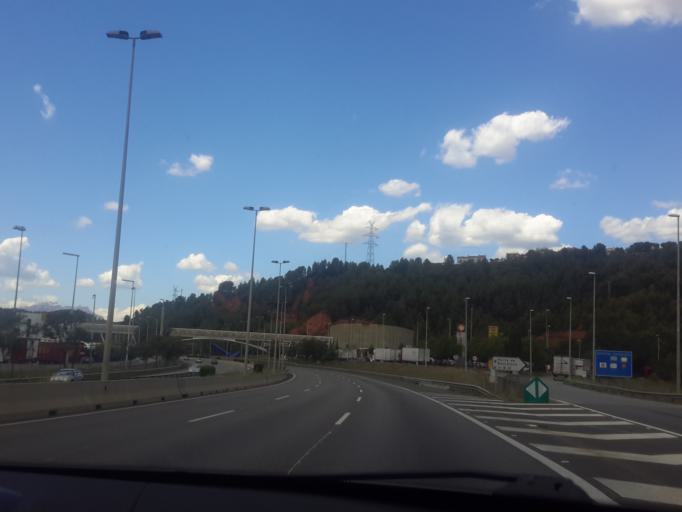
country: ES
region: Catalonia
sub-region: Provincia de Barcelona
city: Castellbisbal
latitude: 41.4646
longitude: 1.9799
